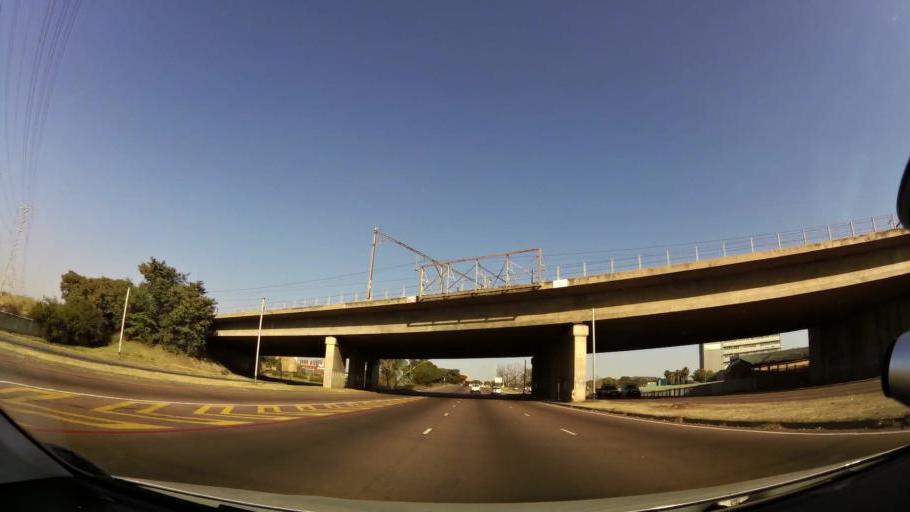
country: ZA
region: Gauteng
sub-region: City of Tshwane Metropolitan Municipality
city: Pretoria
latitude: -25.7360
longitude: 28.1711
